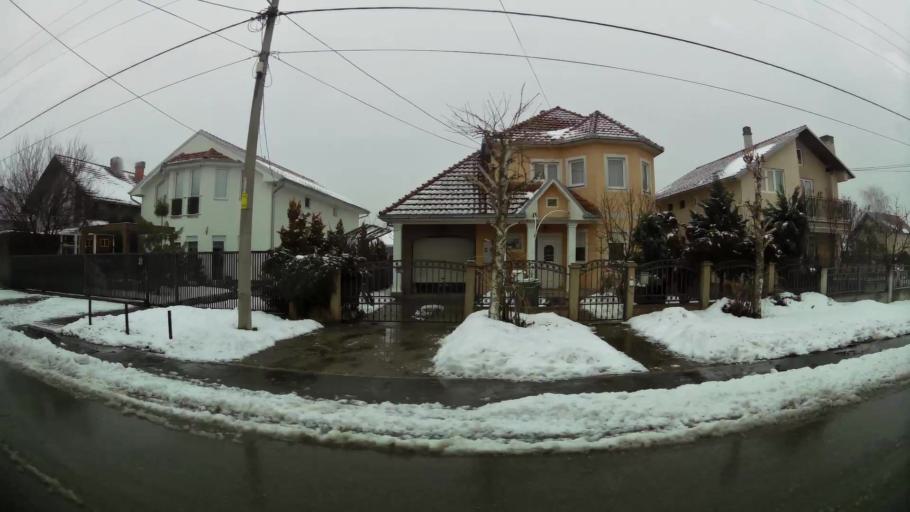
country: RS
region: Central Serbia
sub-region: Belgrade
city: Zemun
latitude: 44.8472
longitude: 20.3449
